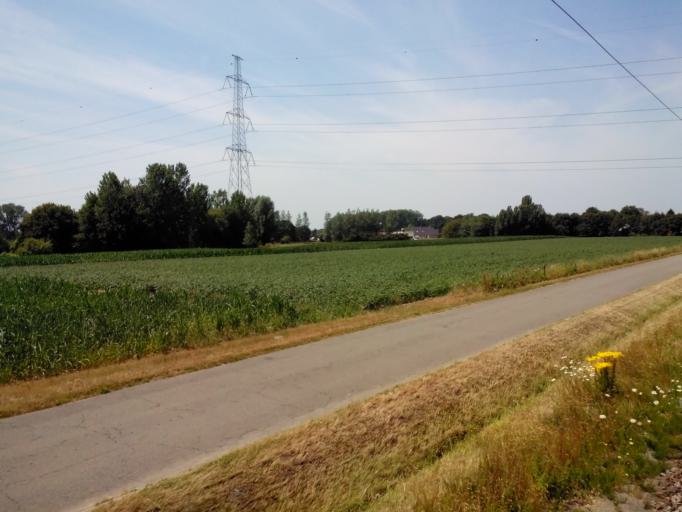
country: BE
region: Flanders
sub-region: Provincie Antwerpen
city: Lint
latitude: 51.1461
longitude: 4.5274
